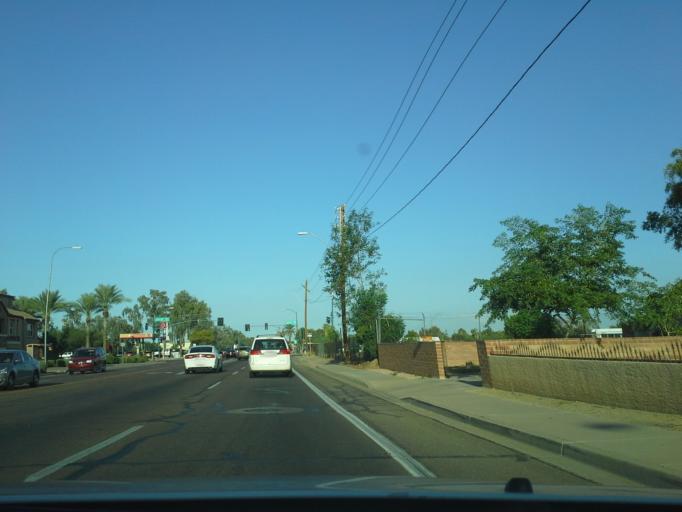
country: US
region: Arizona
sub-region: Maricopa County
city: Phoenix
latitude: 33.3931
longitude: -112.0316
